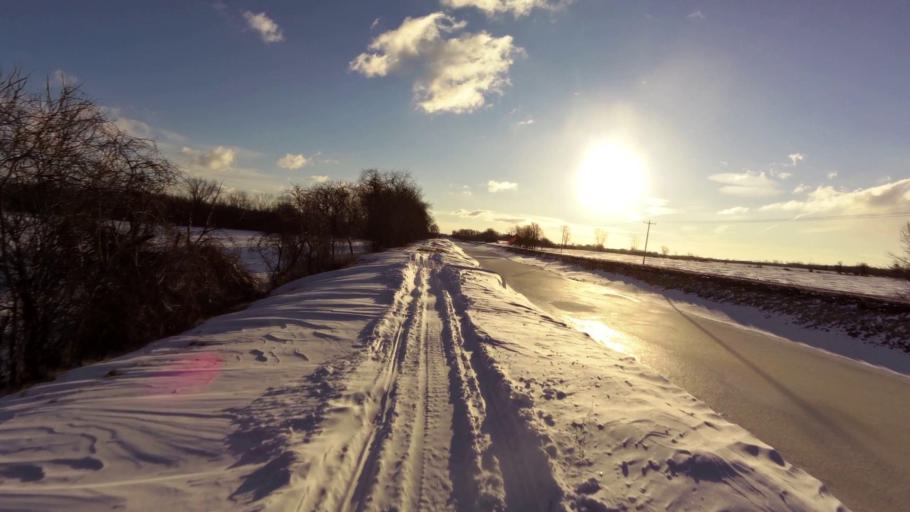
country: US
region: New York
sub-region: Orleans County
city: Medina
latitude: 43.2346
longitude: -78.3508
